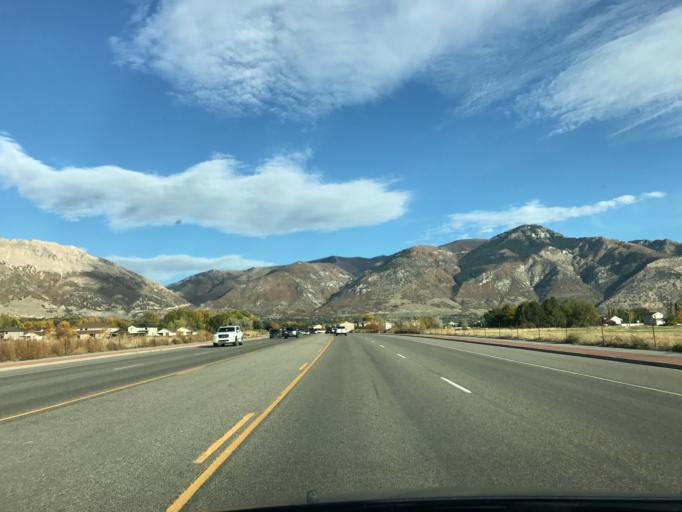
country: US
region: Utah
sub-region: Weber County
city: Pleasant View
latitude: 41.3058
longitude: -111.9892
